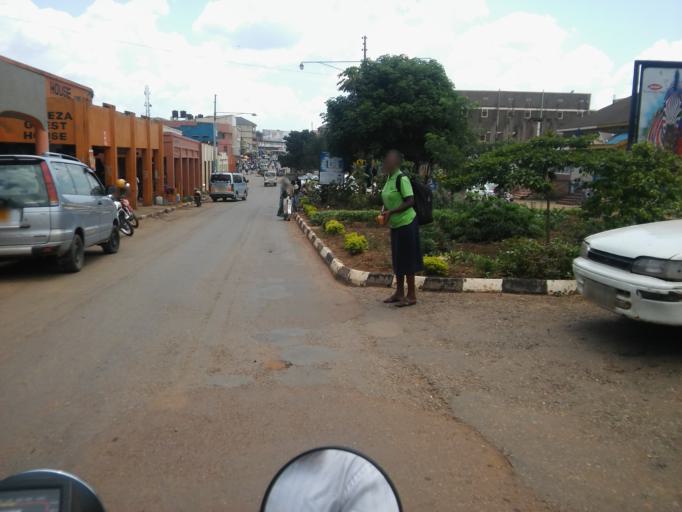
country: UG
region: Eastern Region
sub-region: Mbale District
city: Mbale
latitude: 1.0721
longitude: 34.1793
